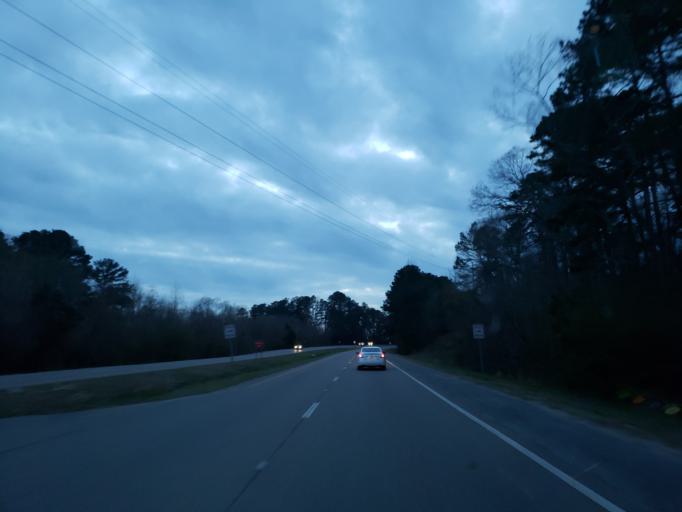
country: US
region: Mississippi
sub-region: Lauderdale County
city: Meridian
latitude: 32.3648
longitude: -88.6586
